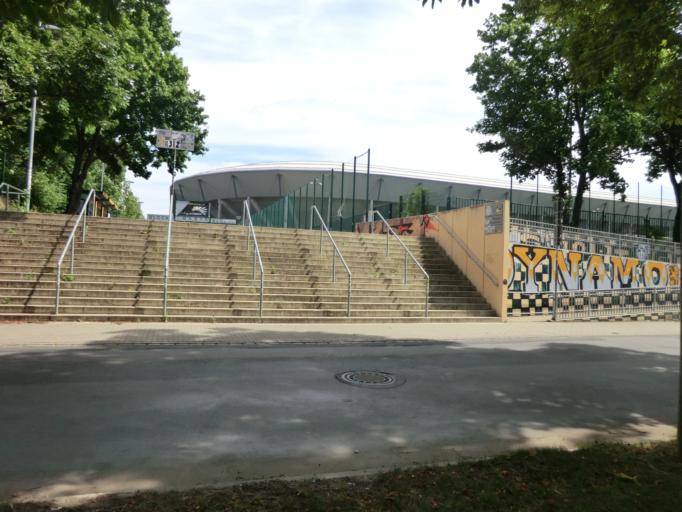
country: DE
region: Saxony
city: Dresden
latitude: 51.0423
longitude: 13.7466
